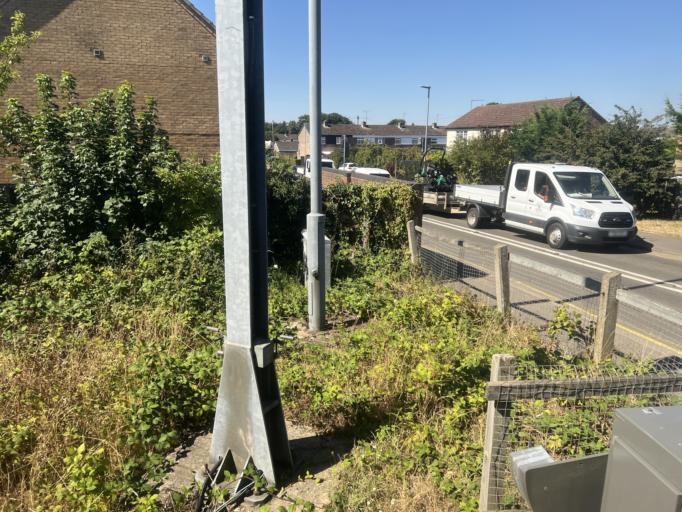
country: GB
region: England
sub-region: Lincolnshire
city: Boston
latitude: 52.9740
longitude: -0.0317
